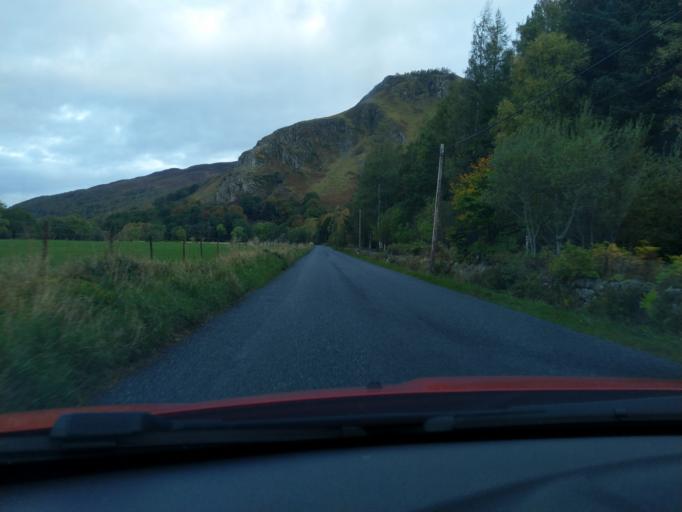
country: GB
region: Scotland
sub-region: Perth and Kinross
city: Aberfeldy
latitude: 56.6996
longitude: -4.1638
